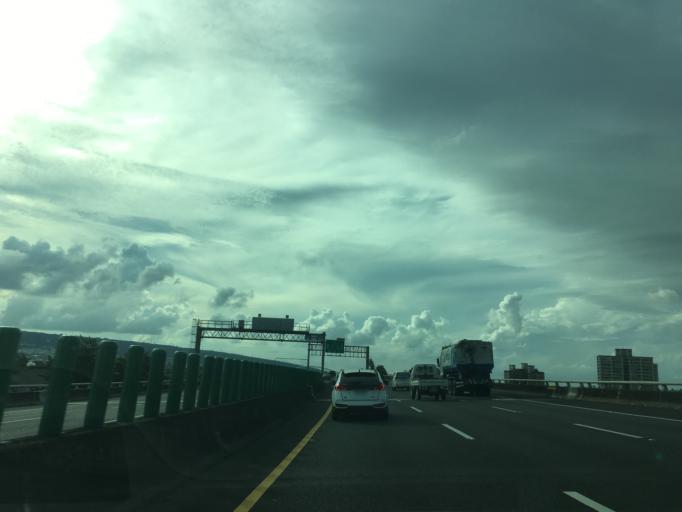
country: TW
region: Taiwan
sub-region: Nantou
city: Nantou
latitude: 23.9089
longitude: 120.7014
